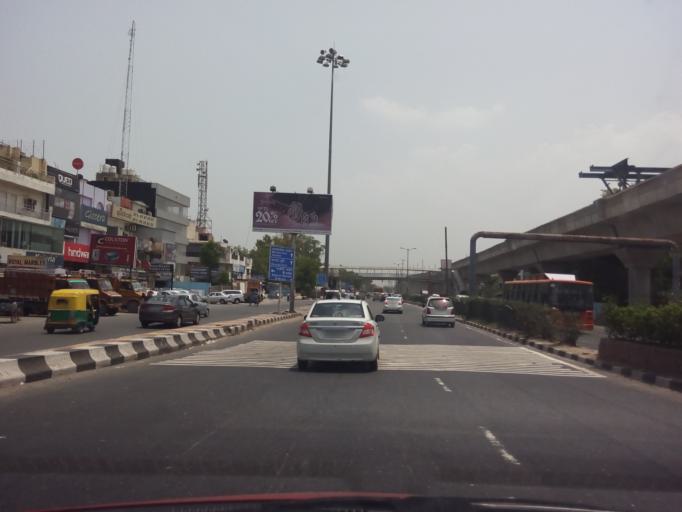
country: IN
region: NCT
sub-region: North West Delhi
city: Pitampura
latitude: 28.6481
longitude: 77.1260
